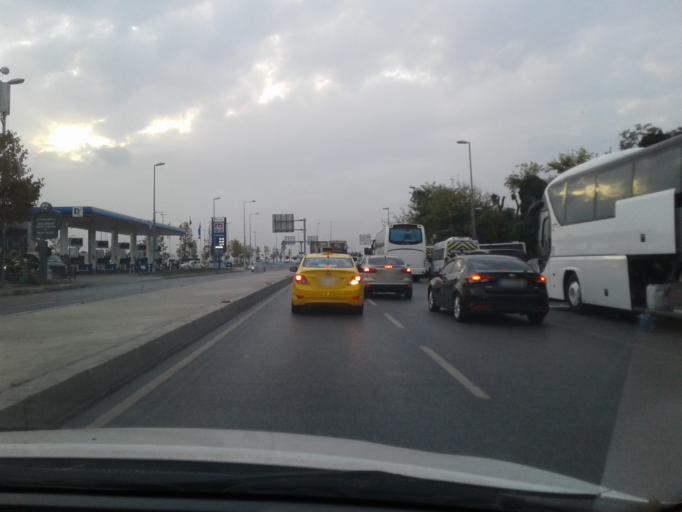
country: TR
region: Istanbul
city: Eminoenue
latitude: 41.0021
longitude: 28.9733
